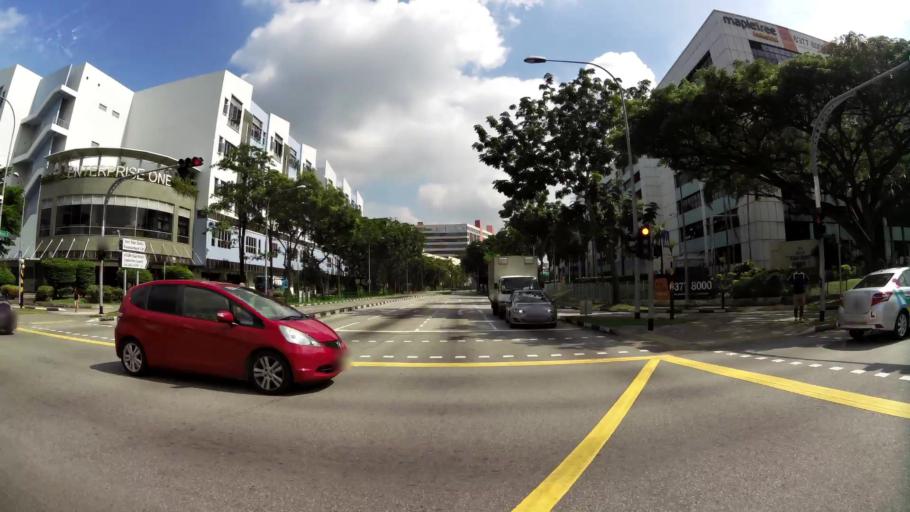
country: SG
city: Singapore
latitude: 1.3319
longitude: 103.9024
